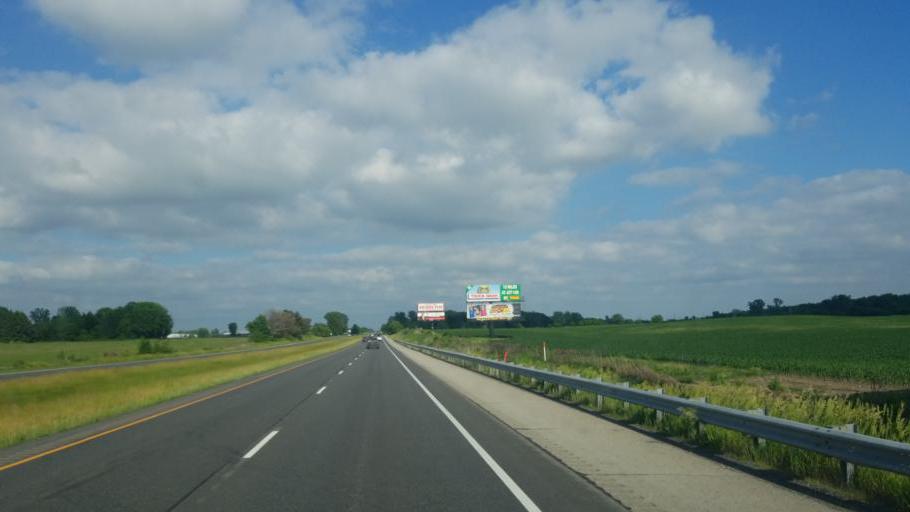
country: US
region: Indiana
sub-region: Whitley County
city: Columbia City
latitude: 41.1383
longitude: -85.4247
